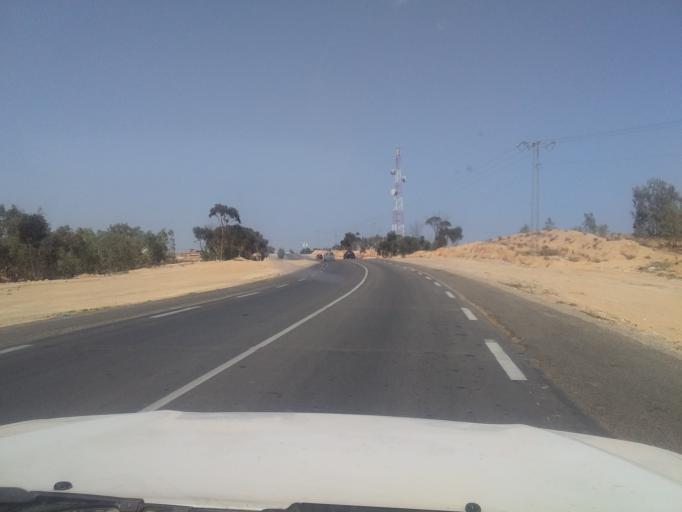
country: TN
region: Madanin
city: Medenine
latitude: 33.5662
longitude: 10.3171
